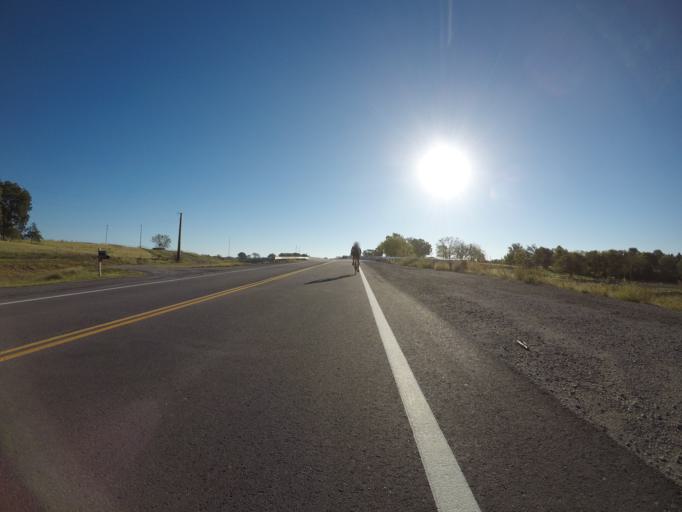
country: US
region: Kansas
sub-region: Douglas County
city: Lawrence
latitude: 39.0005
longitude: -95.1792
